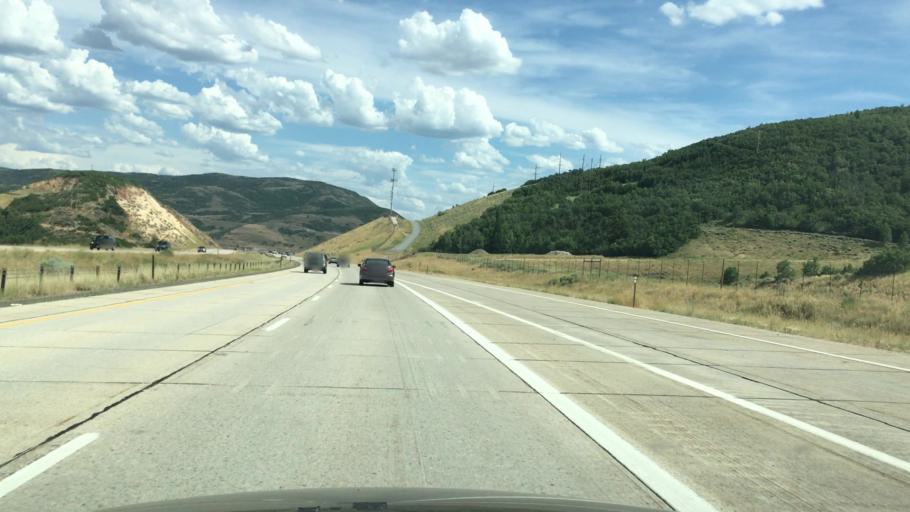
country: US
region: Utah
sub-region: Summit County
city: Park City
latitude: 40.6196
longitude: -111.4373
